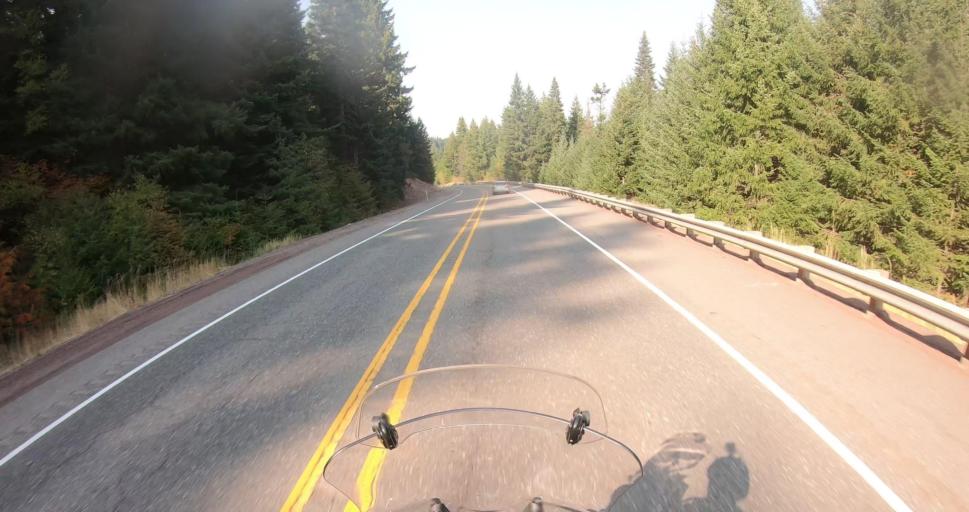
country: US
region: Oregon
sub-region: Hood River County
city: Odell
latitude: 45.4513
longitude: -121.5823
